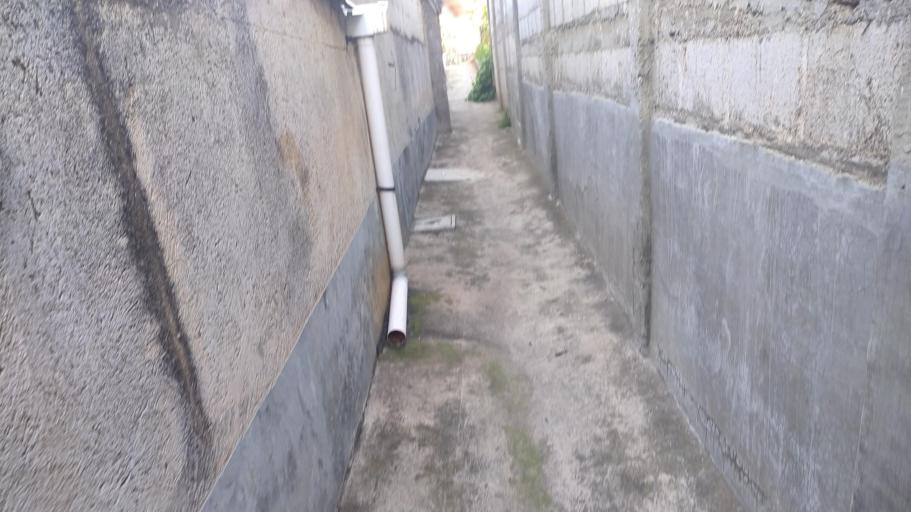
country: GT
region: Quetzaltenango
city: Salcaja
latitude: 14.8709
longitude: -91.4598
